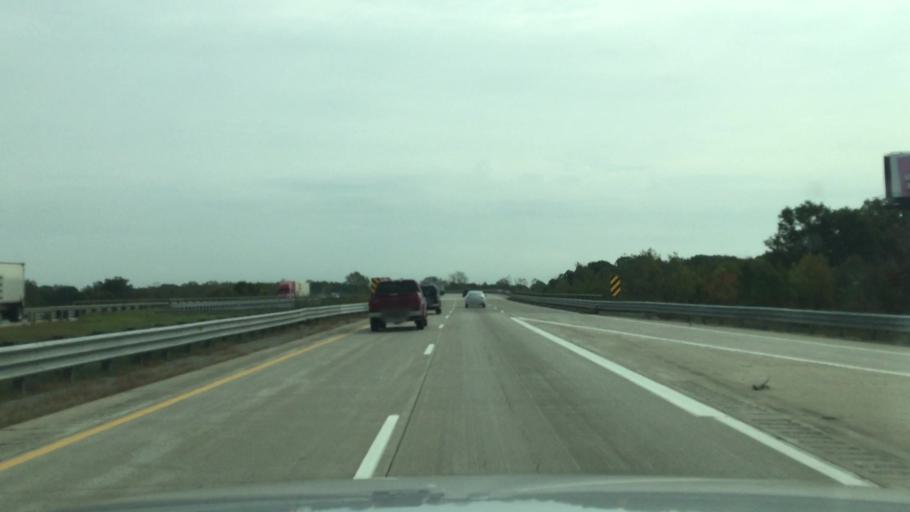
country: US
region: Michigan
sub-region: Genesee County
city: Swartz Creek
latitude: 42.9648
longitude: -83.8029
